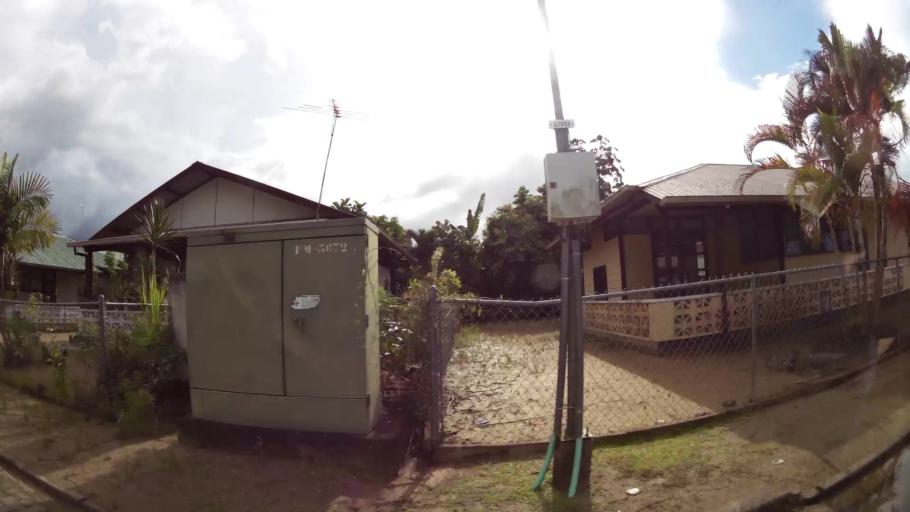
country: SR
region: Paramaribo
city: Paramaribo
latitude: 5.8448
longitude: -55.2119
